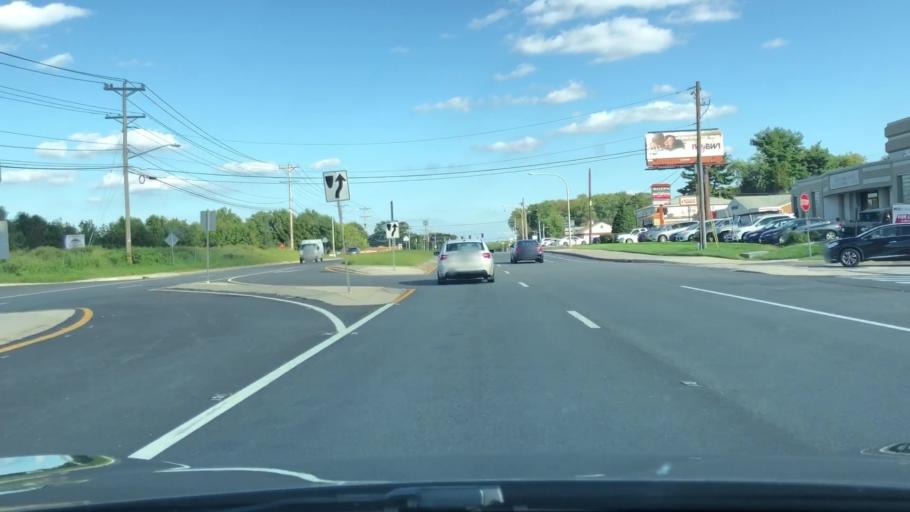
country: US
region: Delaware
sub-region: New Castle County
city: Claymont
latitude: 39.8231
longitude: -75.4900
